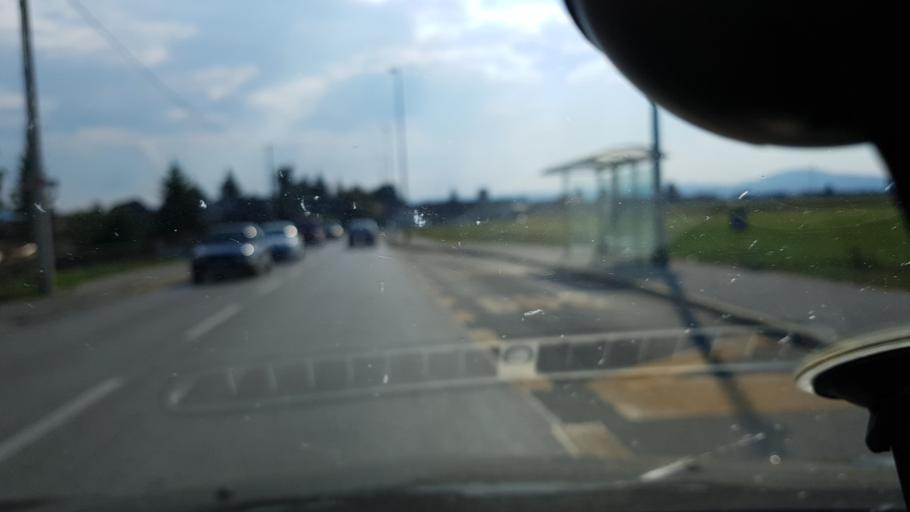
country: HR
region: Zagrebacka
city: Brdovec
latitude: 45.8616
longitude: 15.7868
